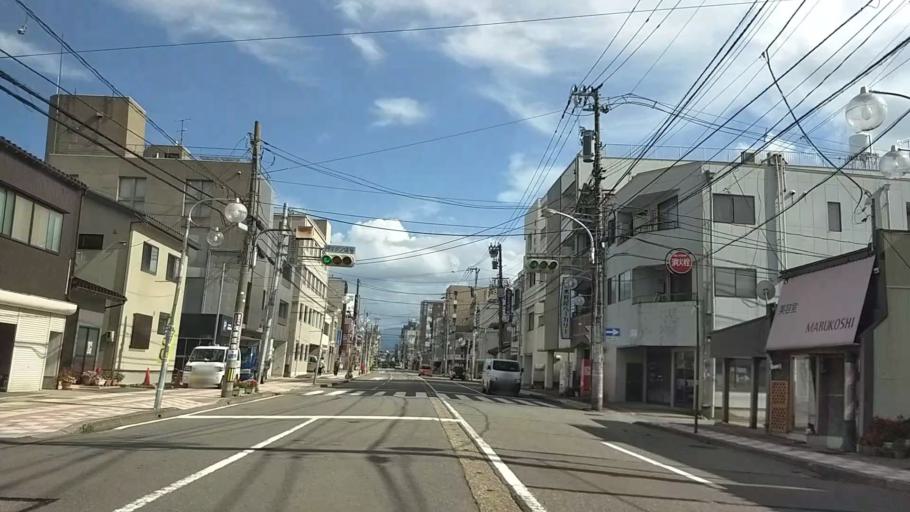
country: JP
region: Ishikawa
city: Kanazawa-shi
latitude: 36.5571
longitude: 136.6685
